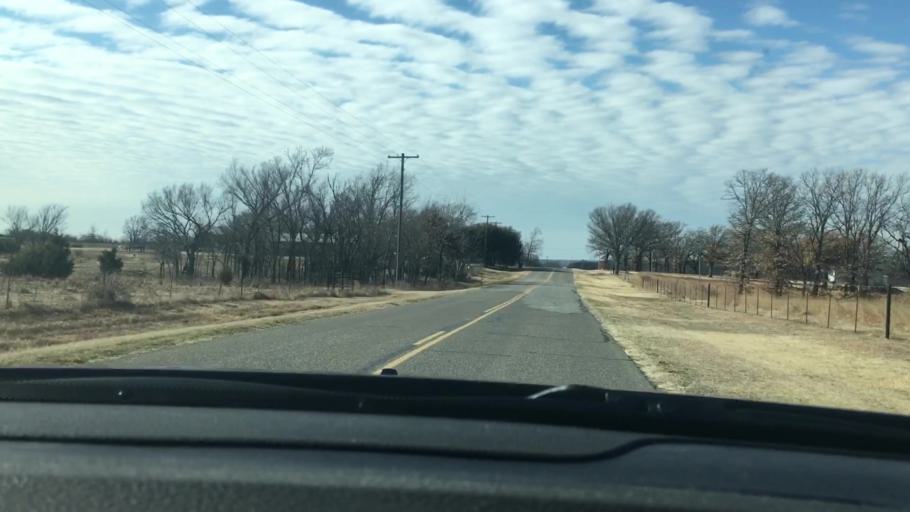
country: US
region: Oklahoma
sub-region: Garvin County
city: Pauls Valley
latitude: 34.7385
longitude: -97.1349
